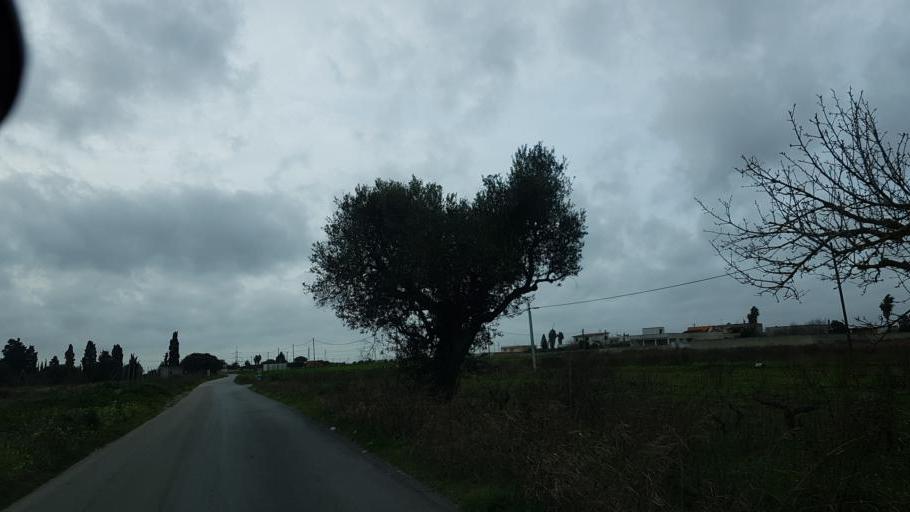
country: IT
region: Apulia
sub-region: Provincia di Brindisi
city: Brindisi
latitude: 40.6103
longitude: 17.9263
